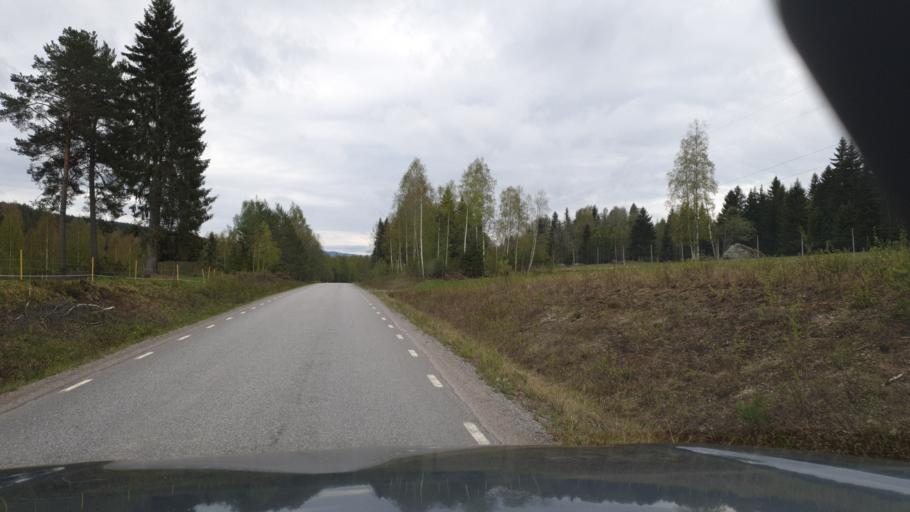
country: SE
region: Gaevleborg
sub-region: Ljusdals Kommun
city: Jaervsoe
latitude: 61.7335
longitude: 16.2816
